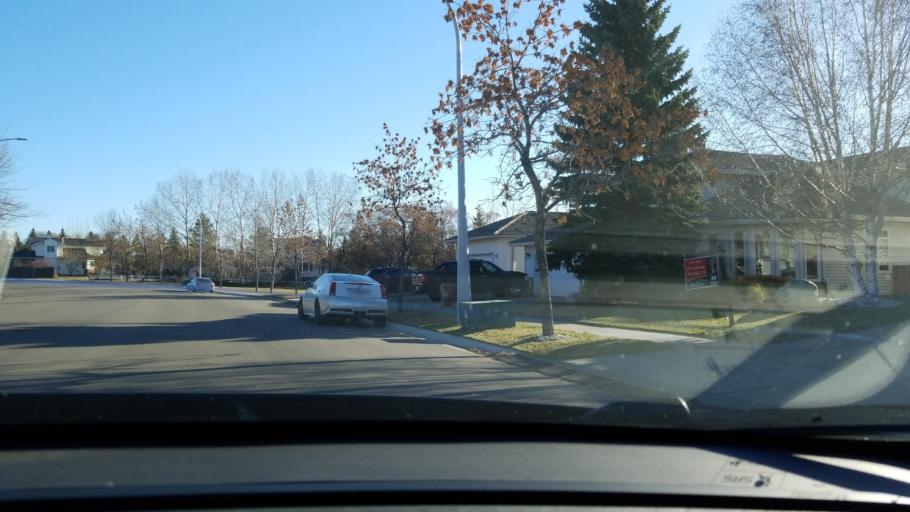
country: CA
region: Alberta
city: Sherwood Park
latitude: 53.5230
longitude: -113.2760
